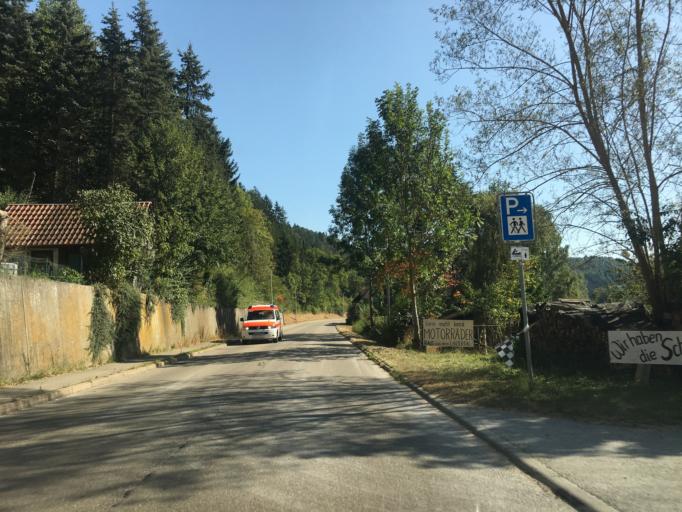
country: DE
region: Baden-Wuerttemberg
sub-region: Tuebingen Region
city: Munsingen
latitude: 48.3594
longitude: 9.4816
